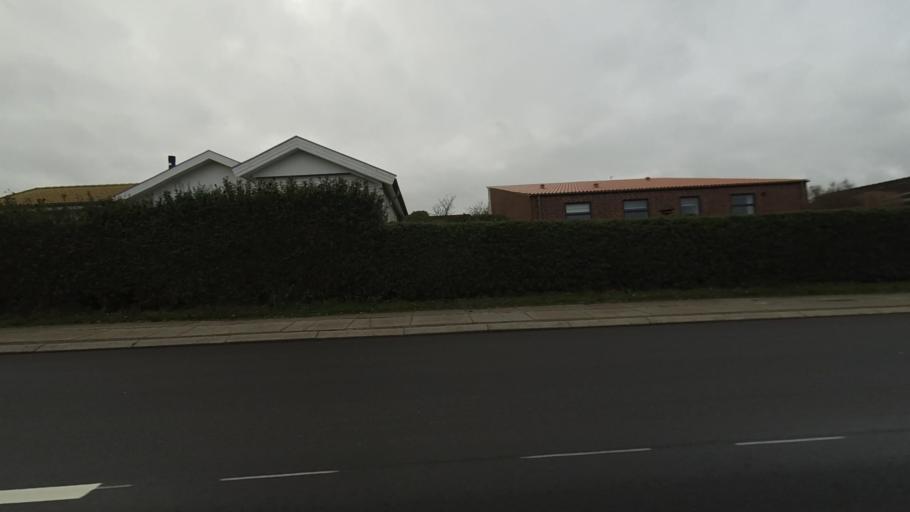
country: DK
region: Central Jutland
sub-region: Arhus Kommune
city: Marslet
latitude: 56.1063
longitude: 10.1753
